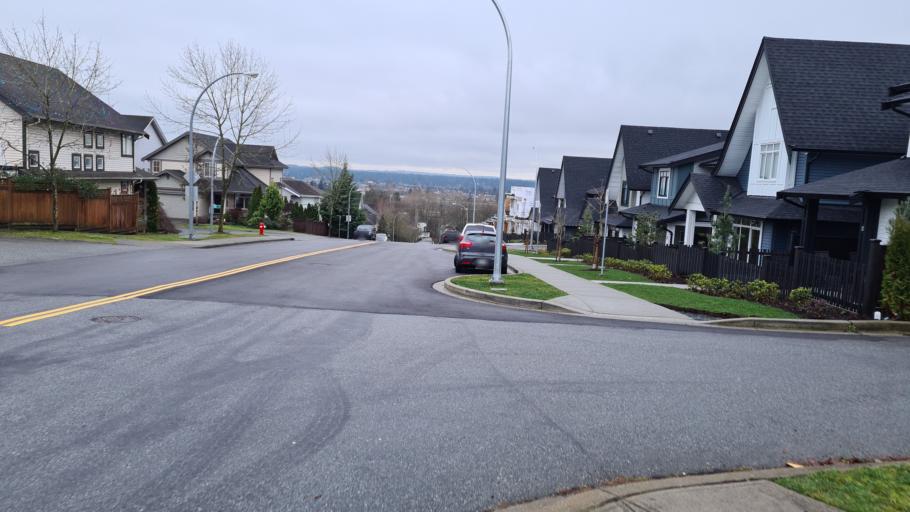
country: CA
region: British Columbia
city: Langley
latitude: 49.1287
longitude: -122.6647
